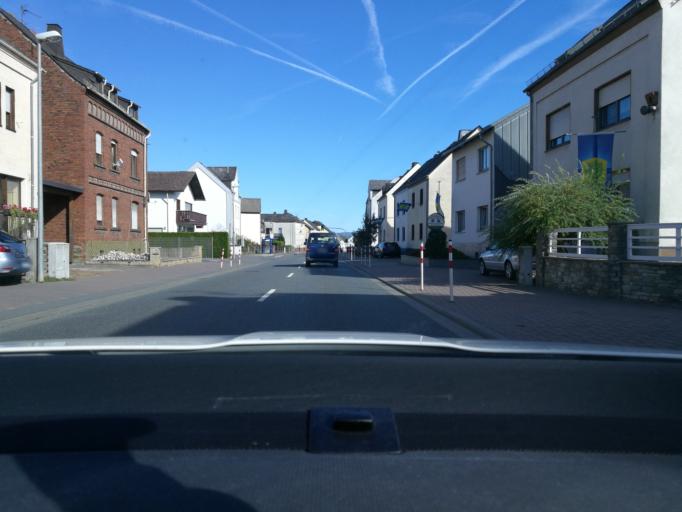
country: DE
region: Hesse
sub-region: Regierungsbezirk Giessen
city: Steeden
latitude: 50.3738
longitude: 8.1178
